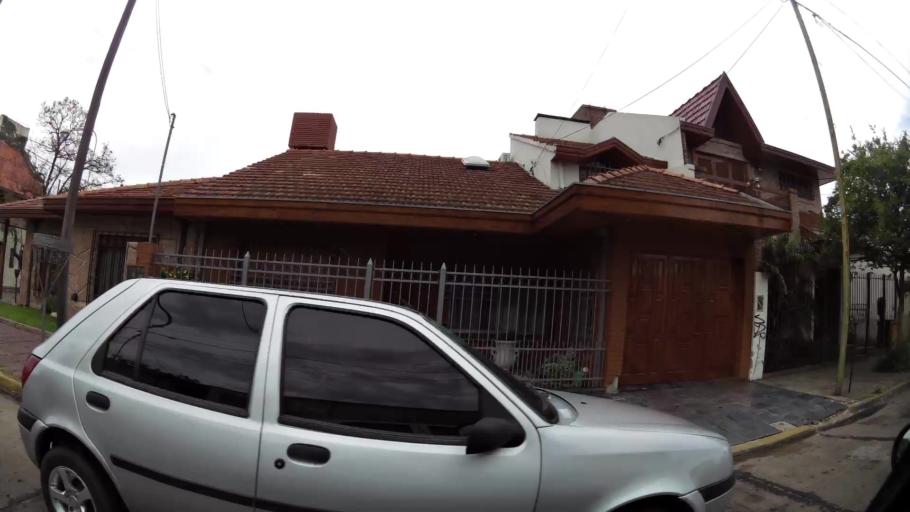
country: AR
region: Buenos Aires
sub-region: Partido de Quilmes
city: Quilmes
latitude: -34.7595
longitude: -58.2163
